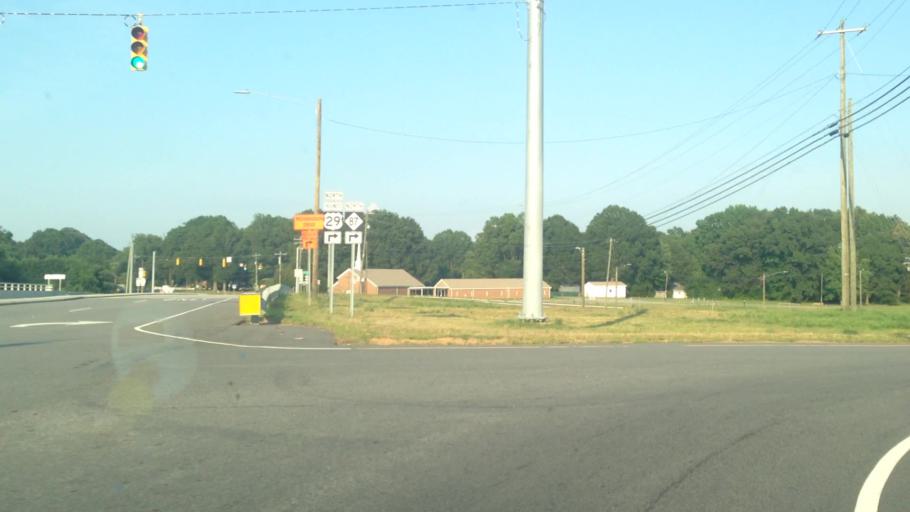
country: US
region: North Carolina
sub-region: Rockingham County
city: Reidsville
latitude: 36.3339
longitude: -79.6936
